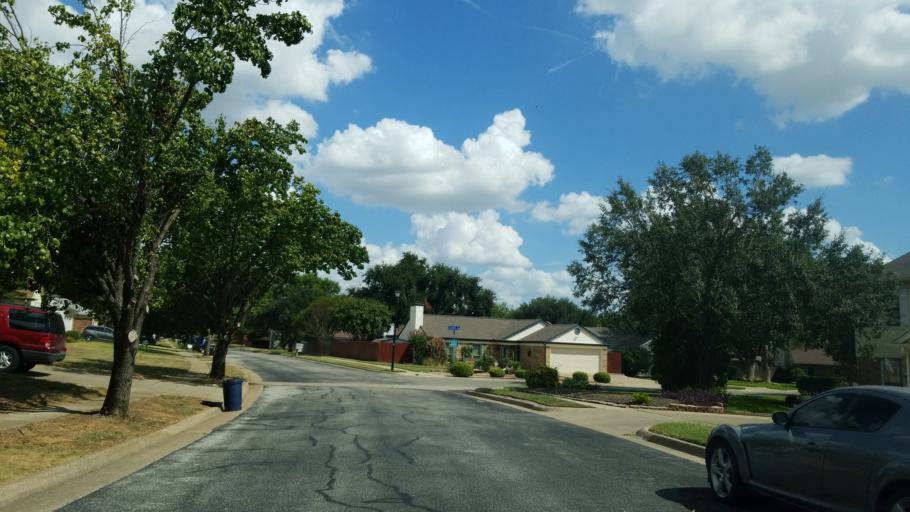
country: US
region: Texas
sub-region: Tarrant County
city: Euless
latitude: 32.8673
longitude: -97.0768
